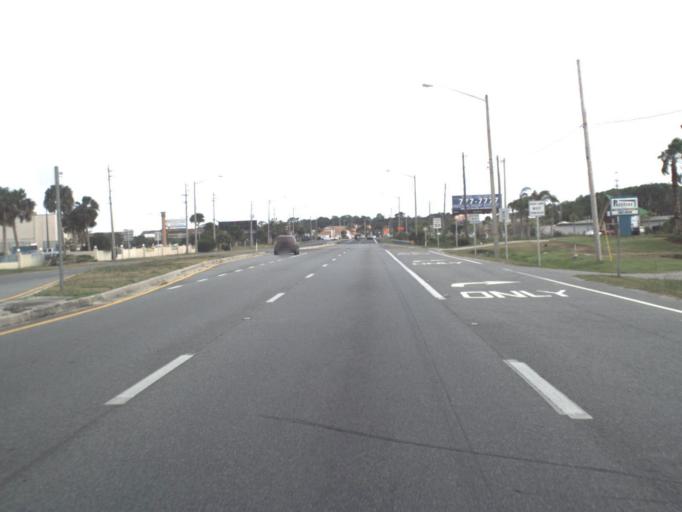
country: US
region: Florida
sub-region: Brevard County
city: Titusville
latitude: 28.5563
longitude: -80.7975
